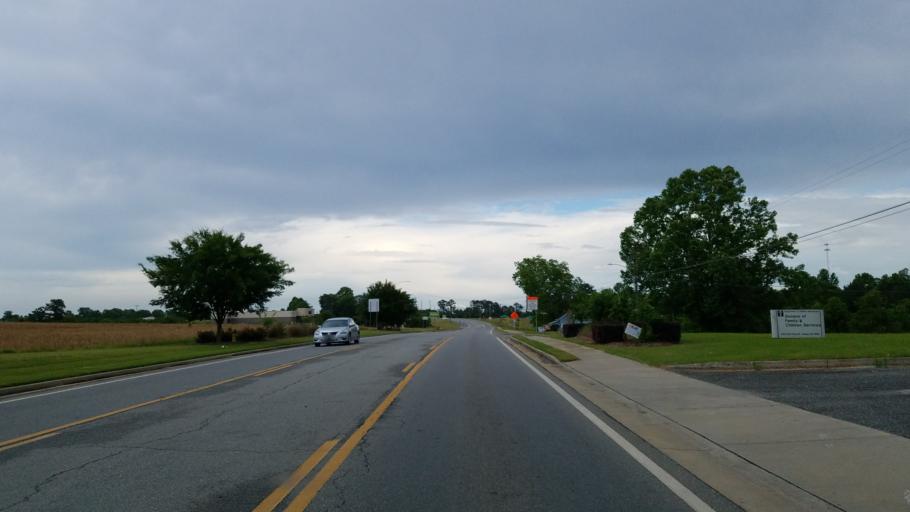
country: US
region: Georgia
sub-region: Dooly County
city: Vienna
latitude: 32.0886
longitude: -83.7771
